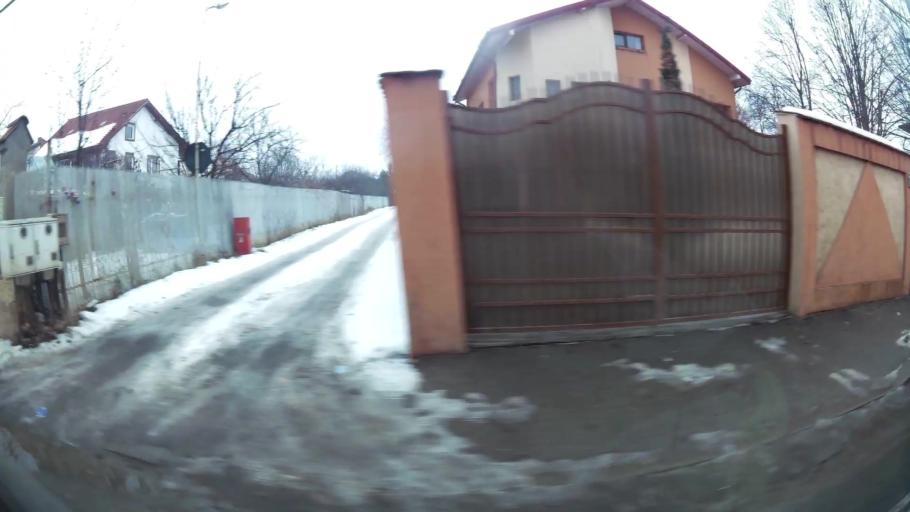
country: RO
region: Ilfov
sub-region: Comuna Chiajna
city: Rosu
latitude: 44.4503
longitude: 26.0018
